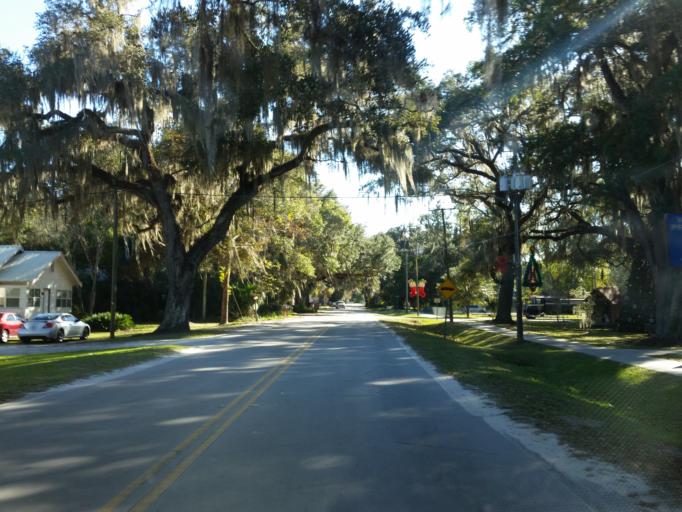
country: US
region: Florida
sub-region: Alachua County
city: Gainesville
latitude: 29.5092
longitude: -82.2795
